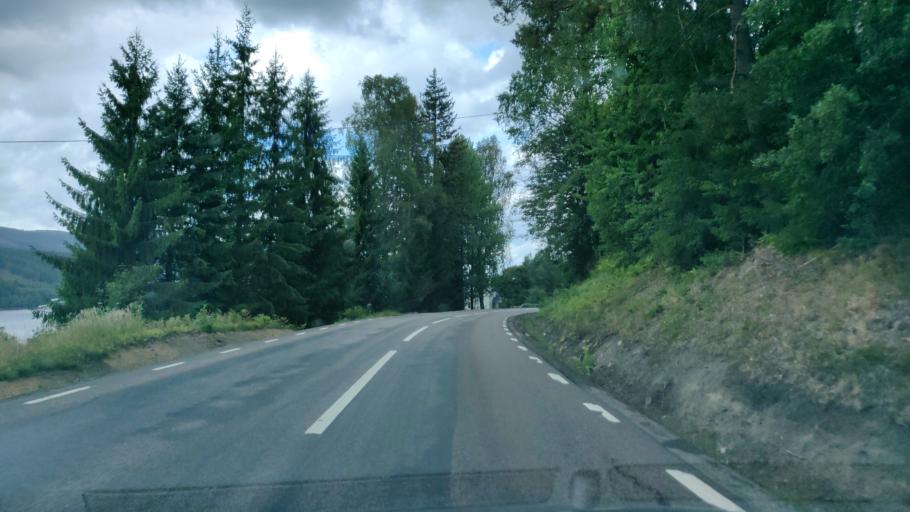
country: SE
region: Vaermland
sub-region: Torsby Kommun
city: Torsby
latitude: 60.6220
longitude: 13.0337
